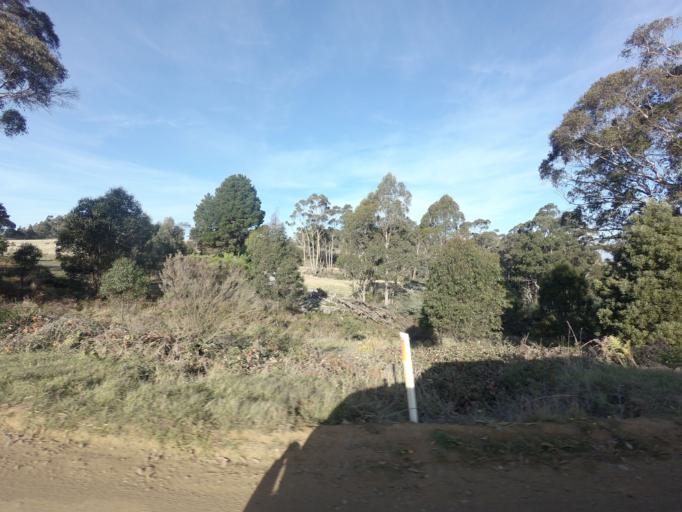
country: AU
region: Tasmania
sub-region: Brighton
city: Bridgewater
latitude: -42.4867
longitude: 147.3859
